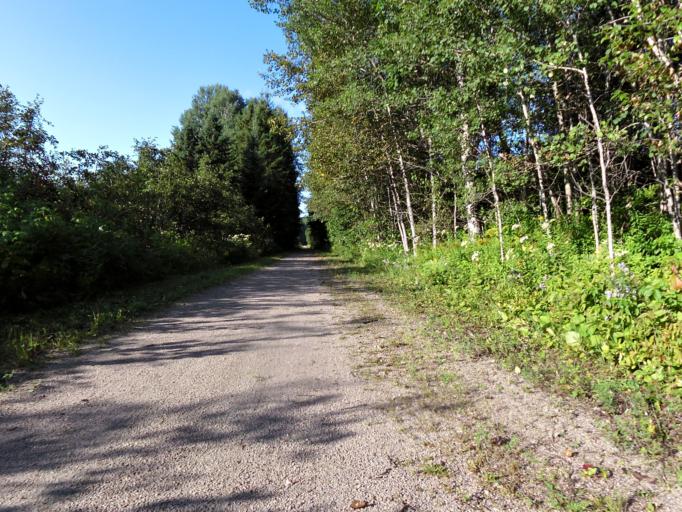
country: CA
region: Quebec
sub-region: Outaouais
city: Maniwaki
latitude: 46.2728
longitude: -76.0141
